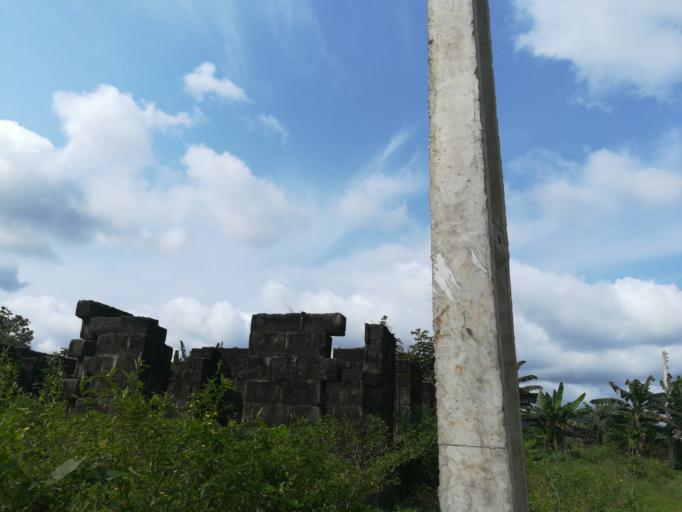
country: NG
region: Rivers
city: Okrika
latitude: 4.7598
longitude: 7.0969
